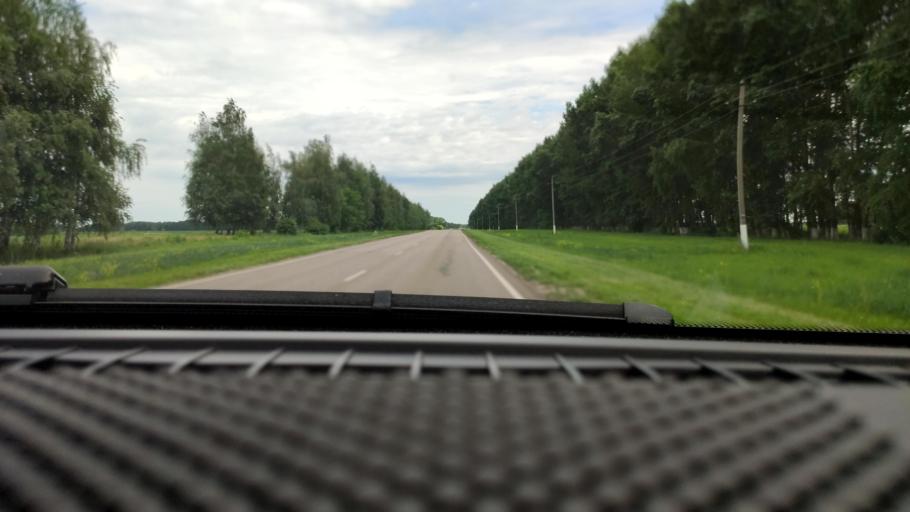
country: RU
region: Voronezj
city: Panino
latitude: 51.6607
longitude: 39.9867
